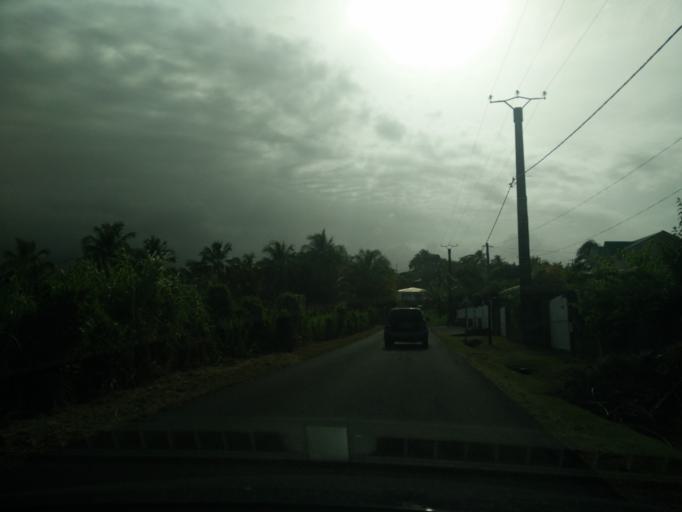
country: GP
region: Guadeloupe
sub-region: Guadeloupe
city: Petit-Bourg
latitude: 16.1267
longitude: -61.5920
